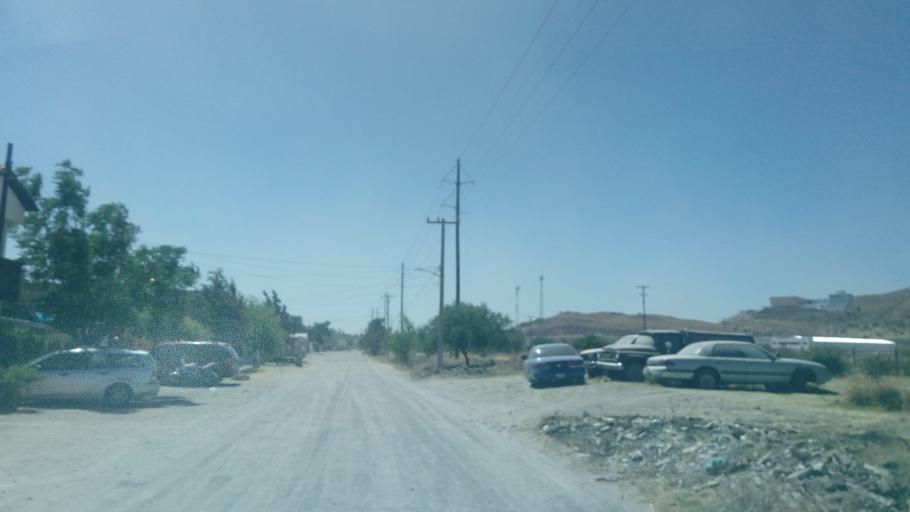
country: MX
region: Durango
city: Victoria de Durango
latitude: 24.0753
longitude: -104.6577
